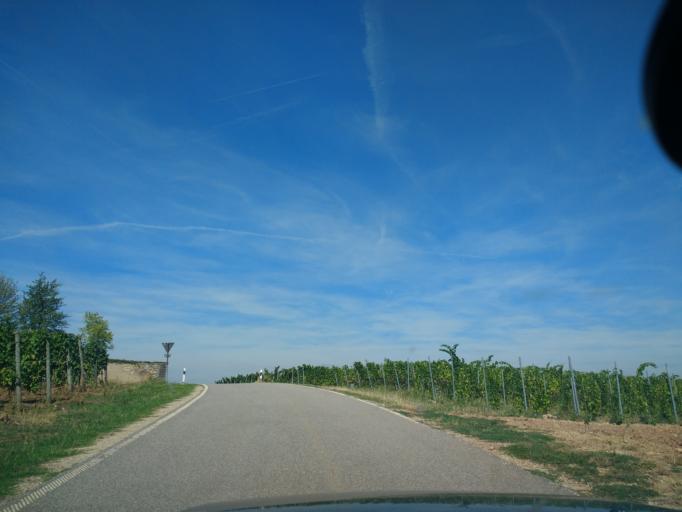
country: DE
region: Rheinland-Pfalz
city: Nittel
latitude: 49.6435
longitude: 6.4525
